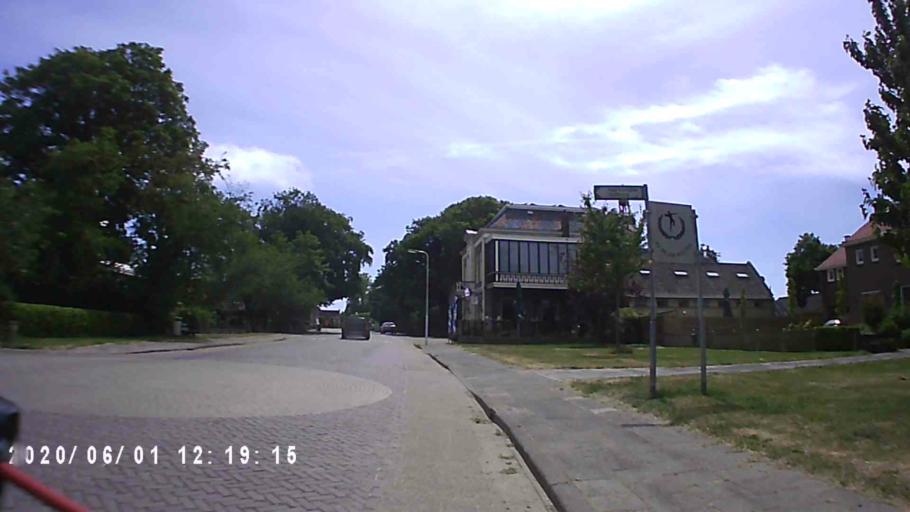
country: NL
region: Friesland
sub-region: Gemeente Harlingen
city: Harlingen
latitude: 53.1308
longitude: 5.4743
